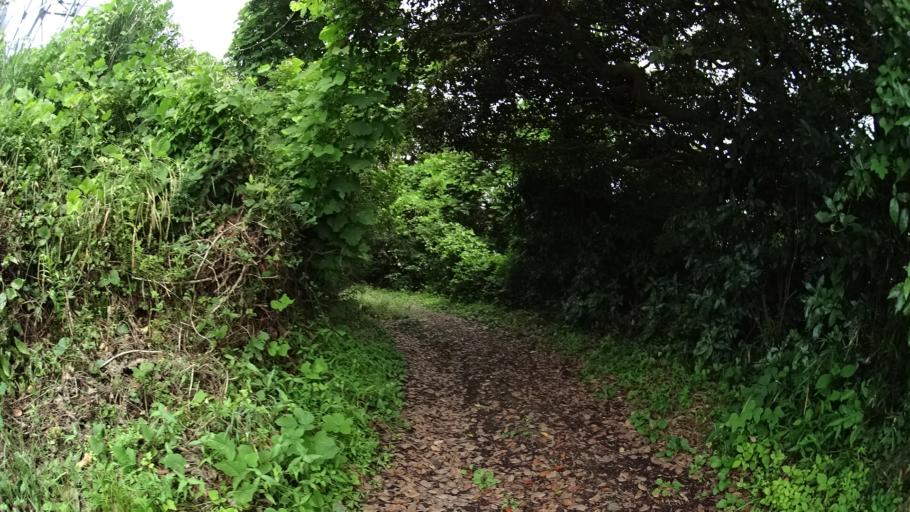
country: JP
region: Kanagawa
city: Yokosuka
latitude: 35.2188
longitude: 139.6619
